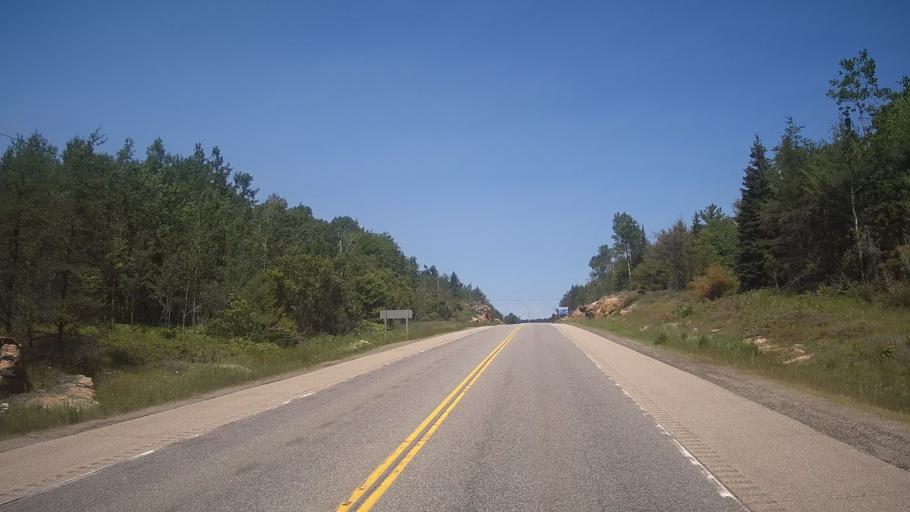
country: CA
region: Ontario
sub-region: Parry Sound District
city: Parry Sound
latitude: 45.6050
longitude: -80.3800
